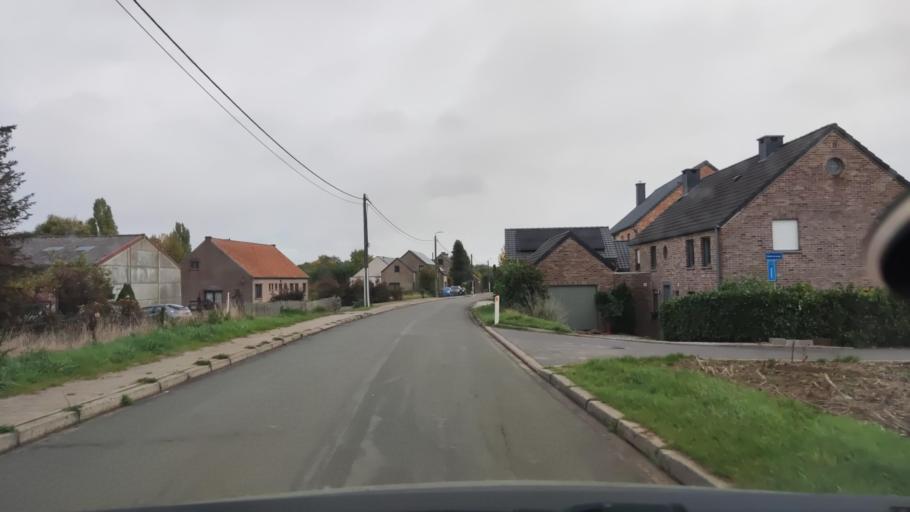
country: BE
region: Flanders
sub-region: Provincie Vlaams-Brabant
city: Hoegaarden
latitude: 50.7579
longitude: 4.8775
